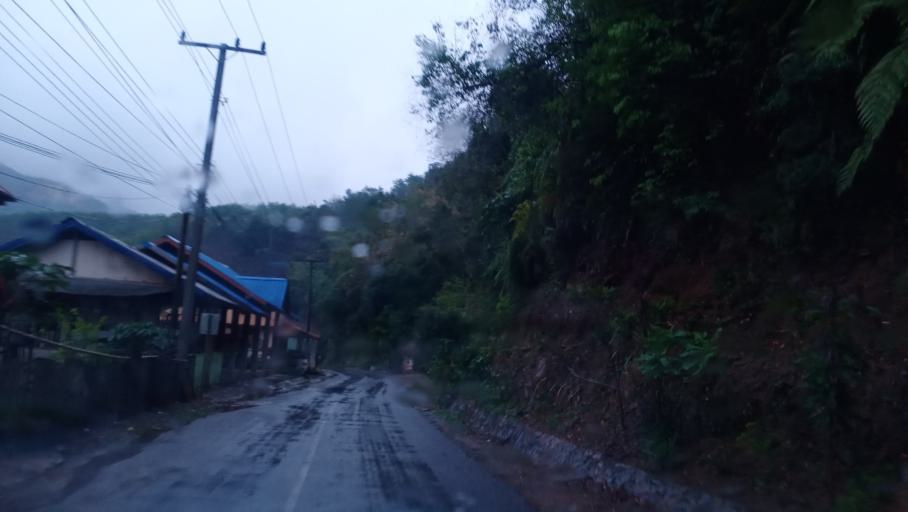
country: LA
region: Phongsali
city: Khoa
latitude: 21.0789
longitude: 102.5009
